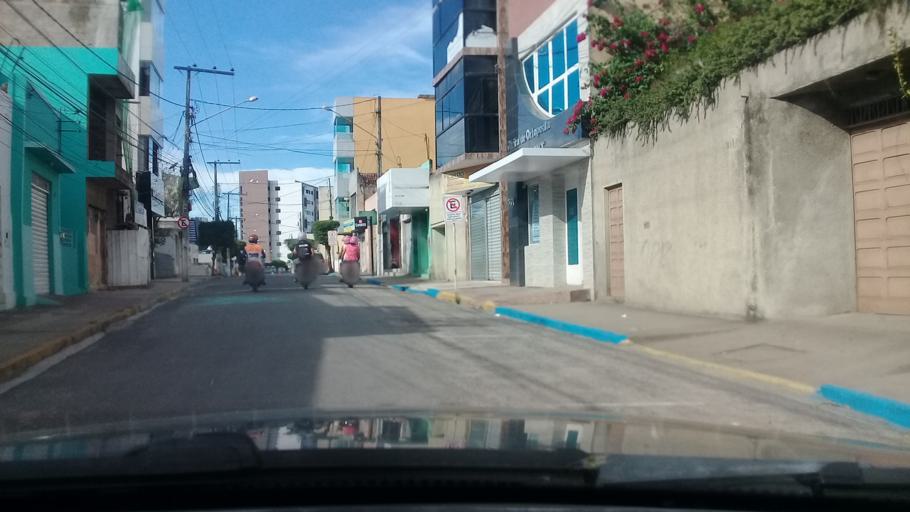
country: BR
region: Pernambuco
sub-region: Vitoria De Santo Antao
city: Vitoria de Santo Antao
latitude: -8.1170
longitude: -35.2953
